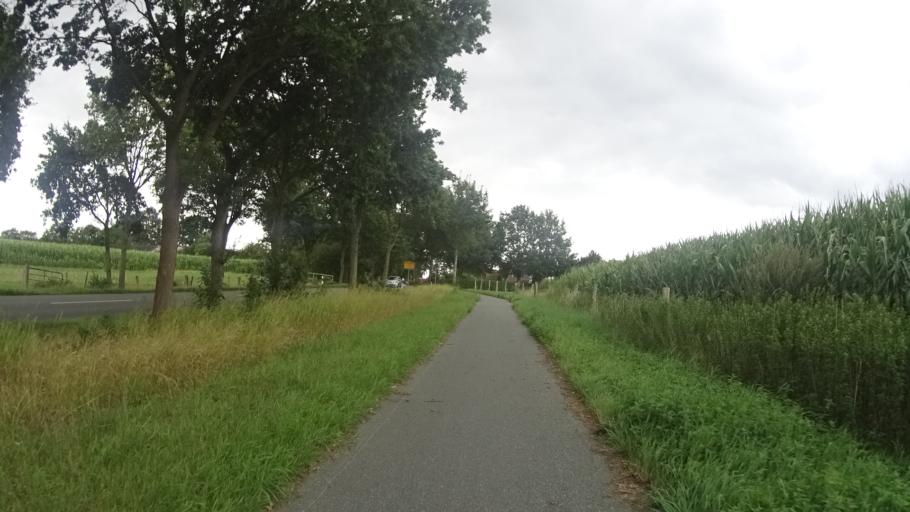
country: DE
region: Lower Saxony
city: Kuhrstedt
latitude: 53.5936
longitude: 8.8108
